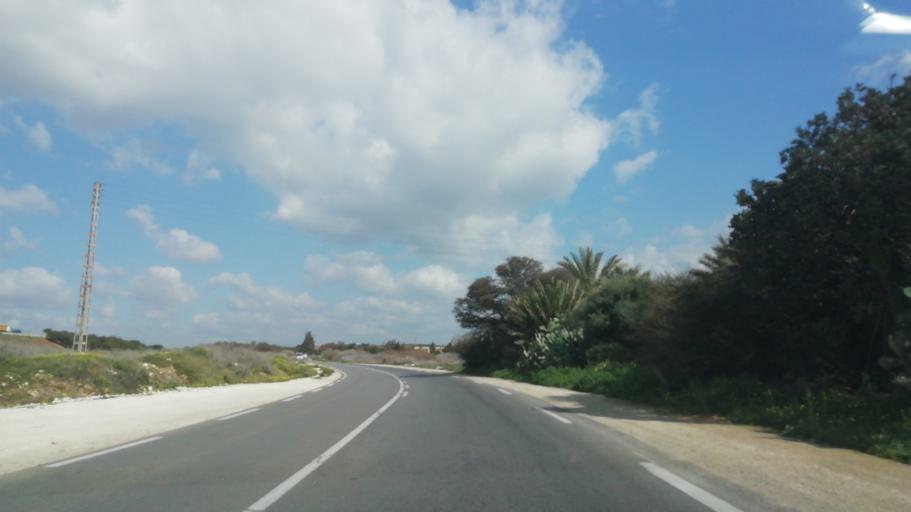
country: DZ
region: Mostaganem
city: Mostaganem
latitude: 35.7008
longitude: 0.2519
